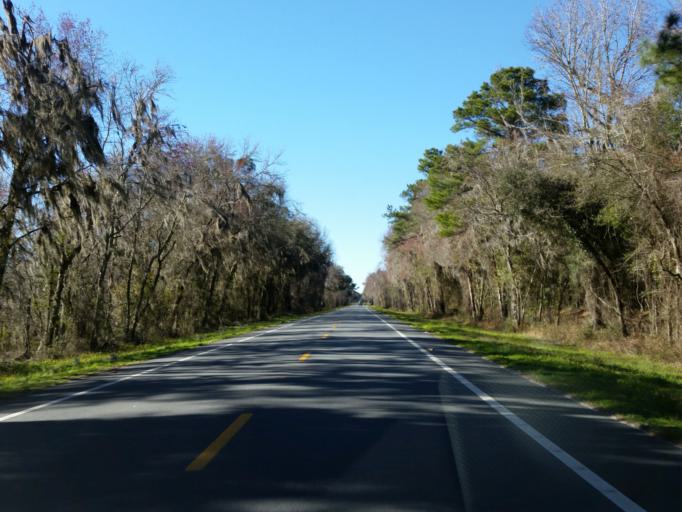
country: US
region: Florida
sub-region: Suwannee County
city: Wellborn
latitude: 30.3786
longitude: -82.8102
